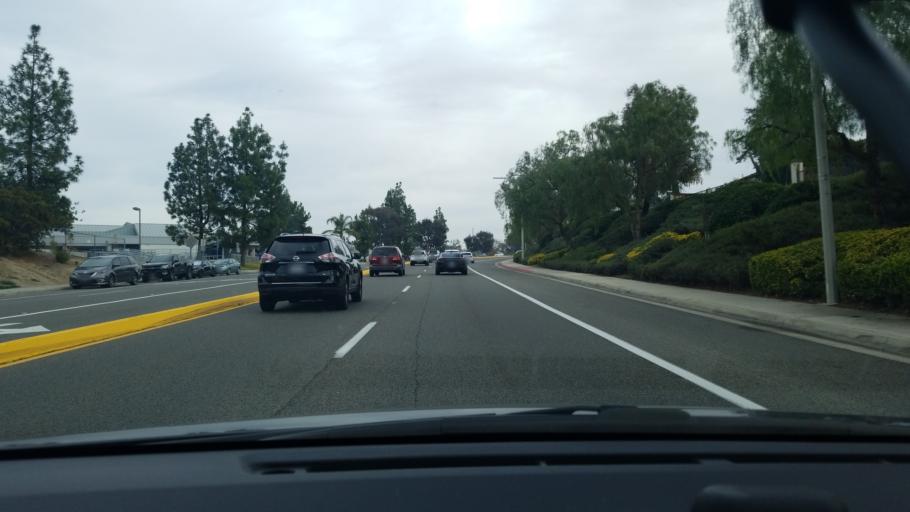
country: US
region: California
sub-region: Riverside County
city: Temecula
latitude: 33.5158
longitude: -117.1298
